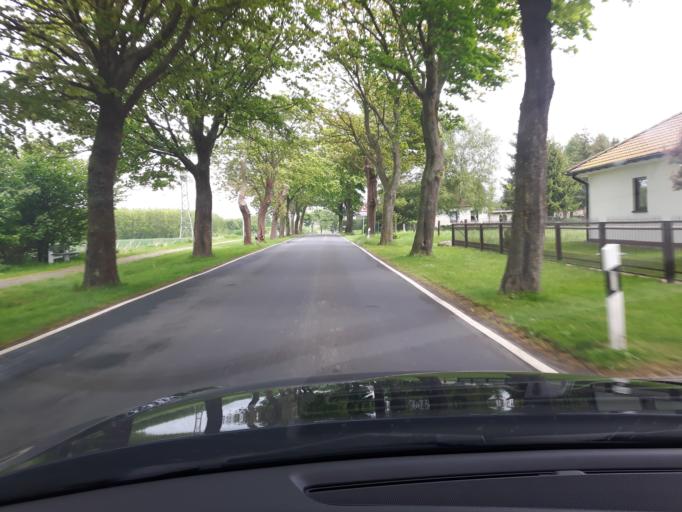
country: DE
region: Mecklenburg-Vorpommern
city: Tribsees
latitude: 54.1664
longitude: 12.7275
